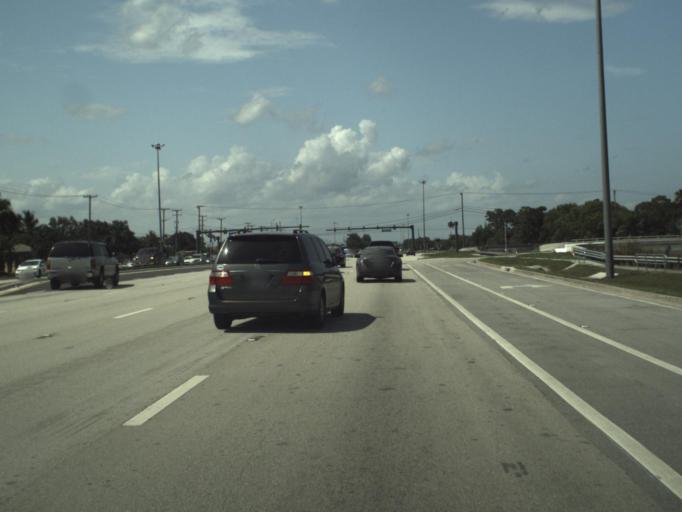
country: US
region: Florida
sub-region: Palm Beach County
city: Wellington
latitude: 26.6693
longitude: -80.2026
